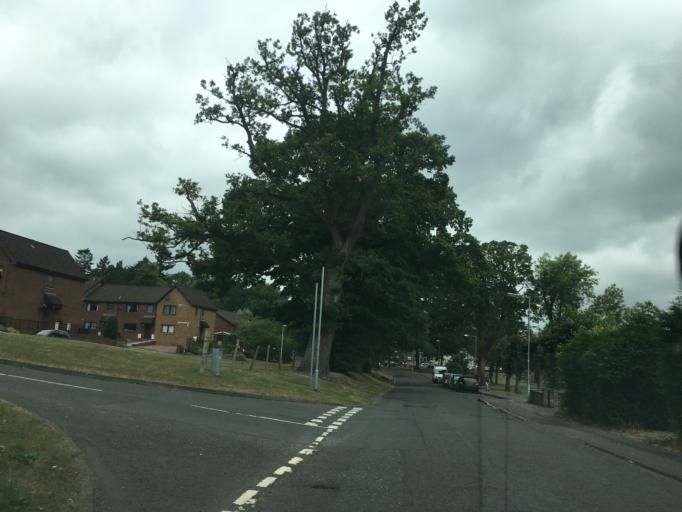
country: GB
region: Scotland
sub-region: The Scottish Borders
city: Peebles
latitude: 55.6424
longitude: -3.1814
